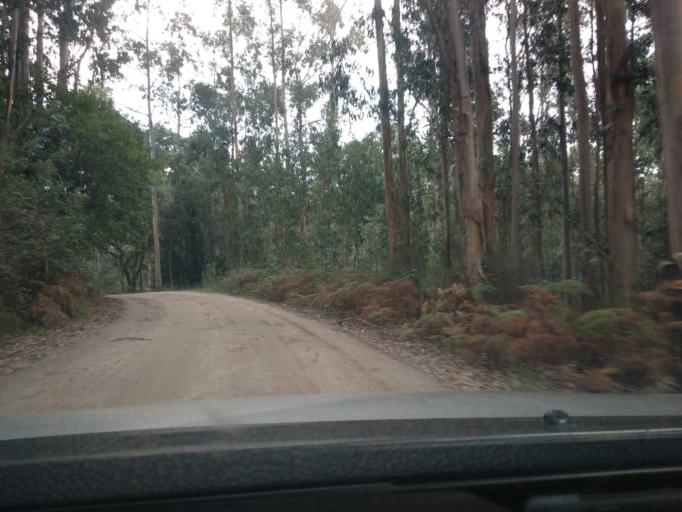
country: ES
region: Galicia
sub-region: Provincia de Pontevedra
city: Moana
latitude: 42.2961
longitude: -8.6928
